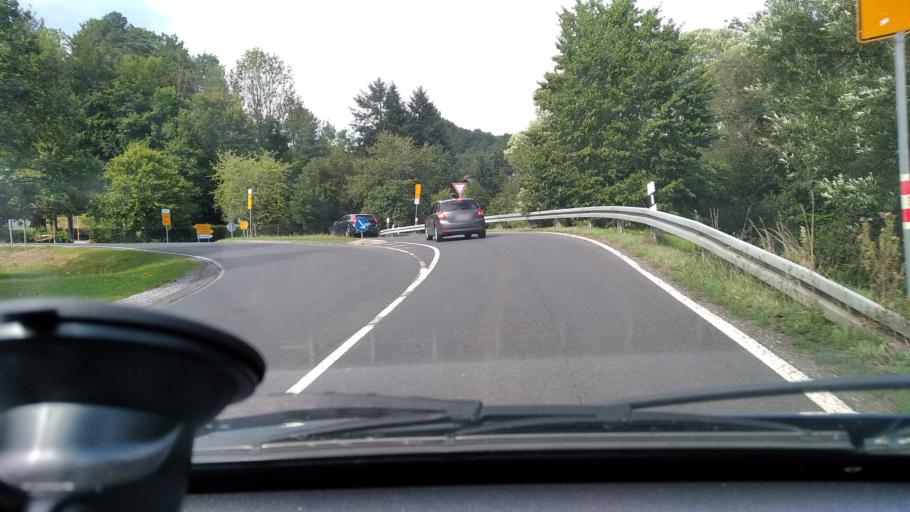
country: DE
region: Hesse
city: Dillenburg
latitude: 50.7415
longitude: 8.3161
